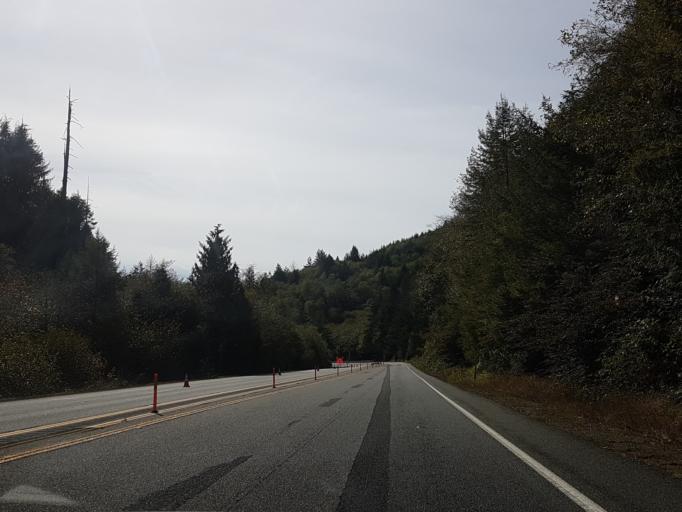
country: US
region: California
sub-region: Del Norte County
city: Bertsch-Oceanview
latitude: 41.4978
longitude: -124.0406
